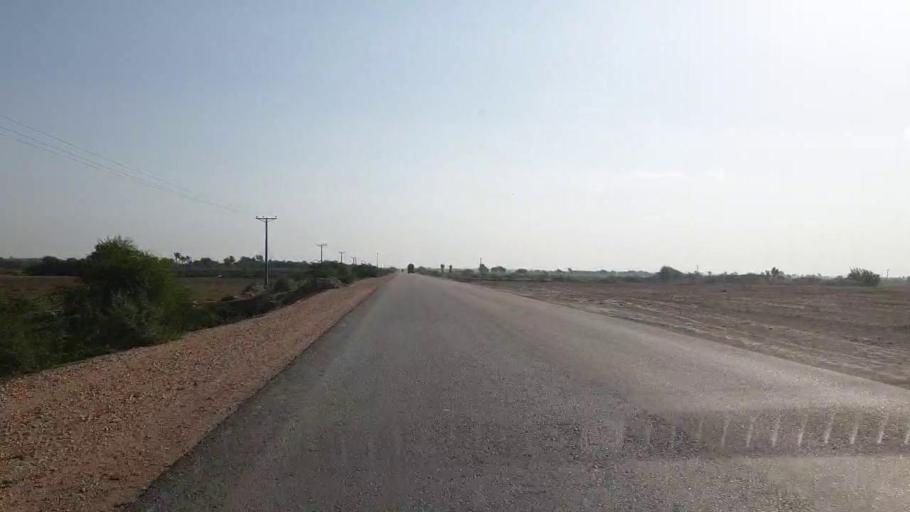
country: PK
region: Sindh
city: Tando Bago
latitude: 24.6576
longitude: 68.9884
